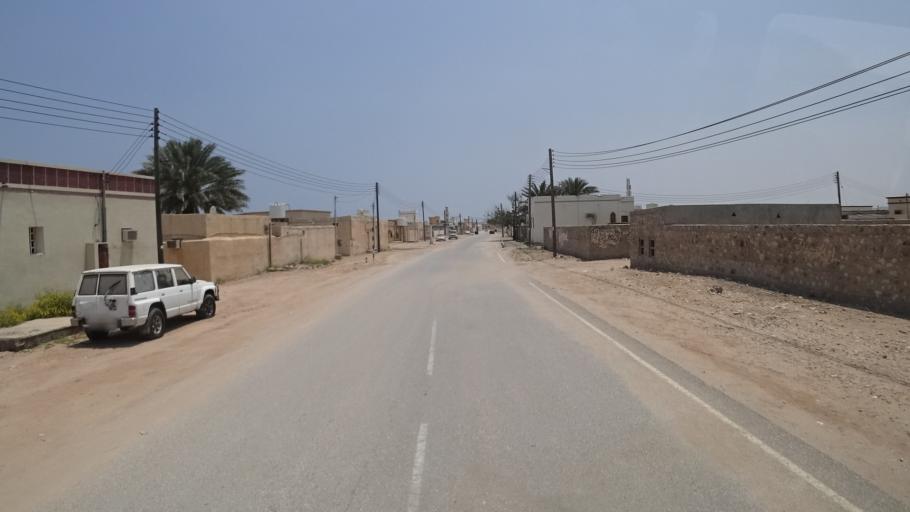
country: OM
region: Ash Sharqiyah
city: Sur
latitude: 22.5192
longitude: 59.7983
